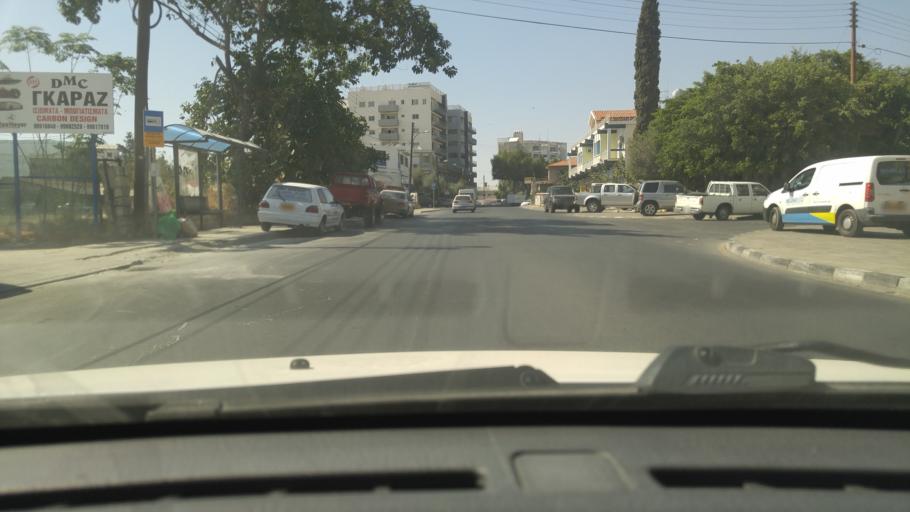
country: CY
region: Limassol
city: Limassol
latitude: 34.6734
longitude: 33.0199
